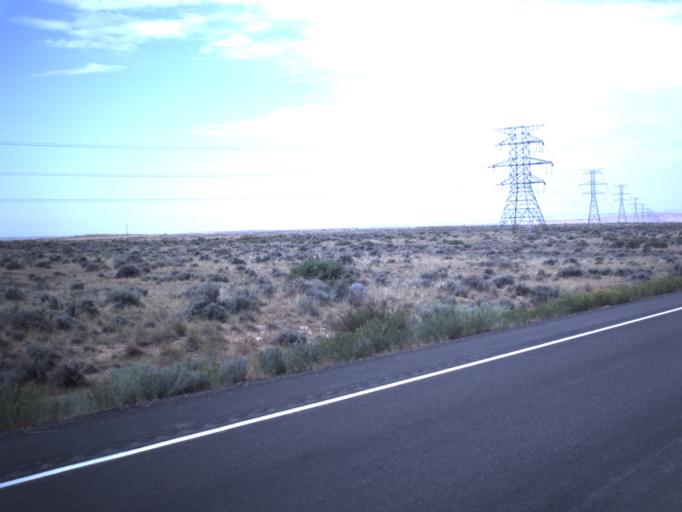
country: US
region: Utah
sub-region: Uintah County
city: Naples
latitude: 40.2274
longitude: -109.4029
